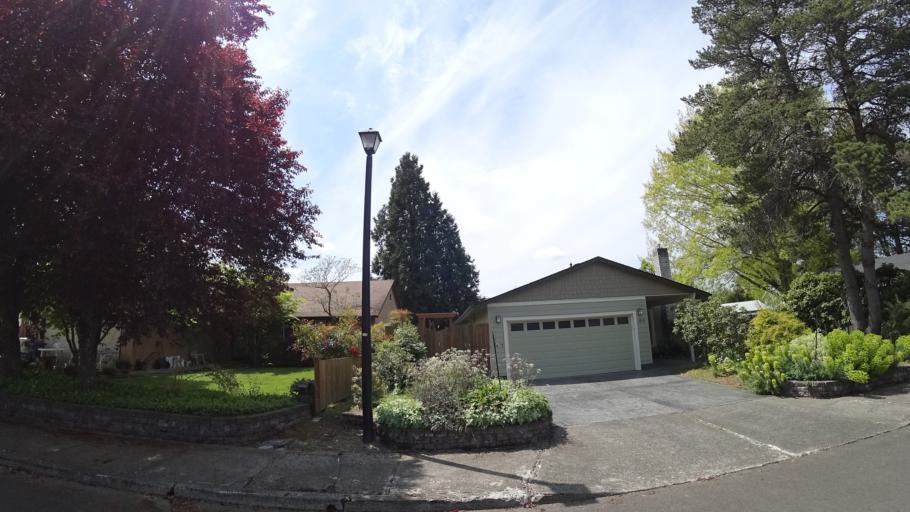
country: US
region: Oregon
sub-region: Washington County
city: Aloha
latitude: 45.4707
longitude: -122.8859
